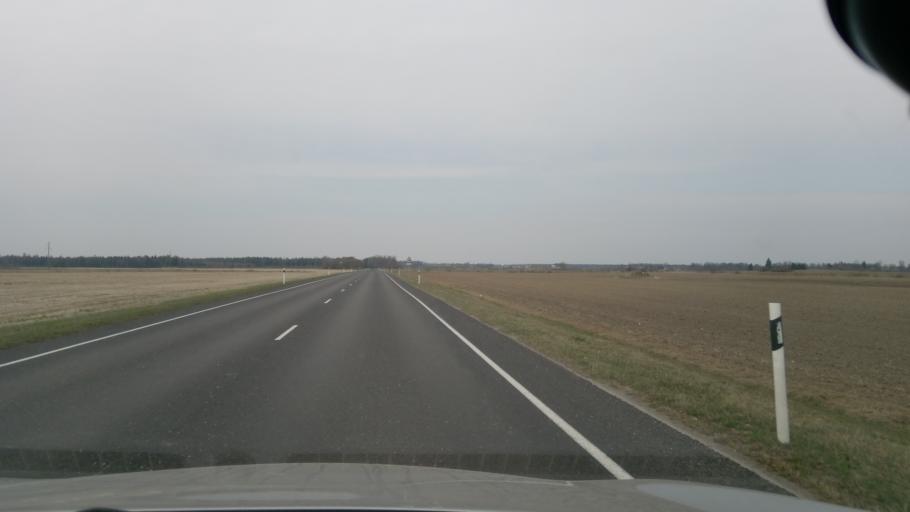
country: EE
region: Viljandimaa
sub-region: Vohma linn
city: Vohma
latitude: 58.7288
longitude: 25.5965
